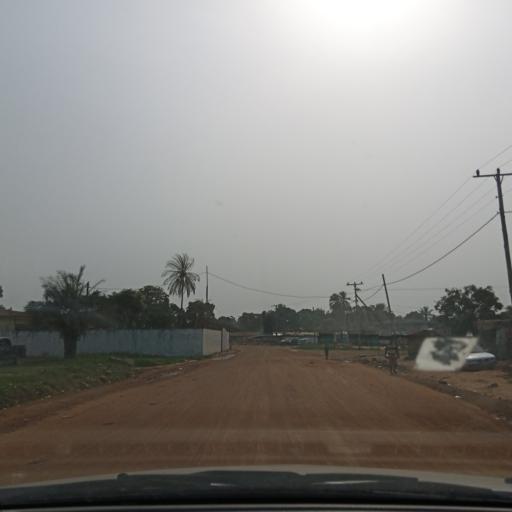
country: LR
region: Montserrado
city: Monrovia
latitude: 6.3384
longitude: -10.7454
